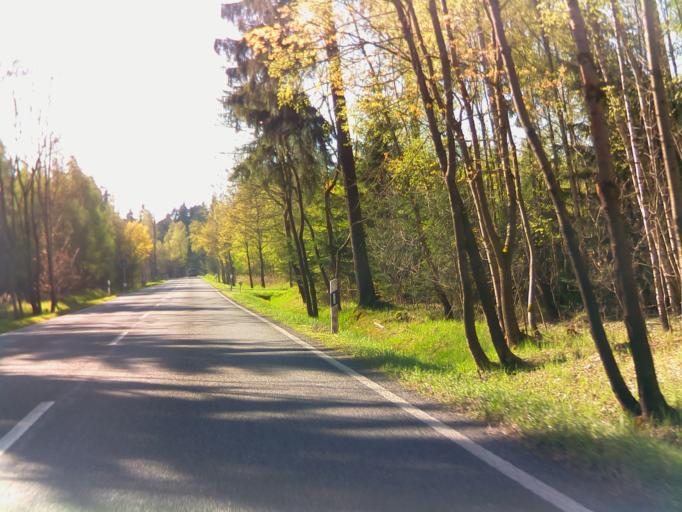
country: DE
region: Thuringia
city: Mossbach
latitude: 50.6697
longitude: 11.7928
